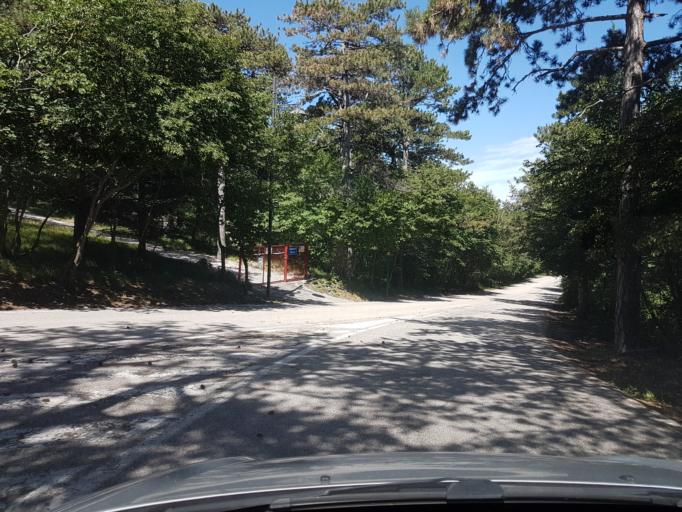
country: IT
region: Friuli Venezia Giulia
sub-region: Provincia di Trieste
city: Prosecco-Contovello
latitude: 45.6942
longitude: 13.7498
